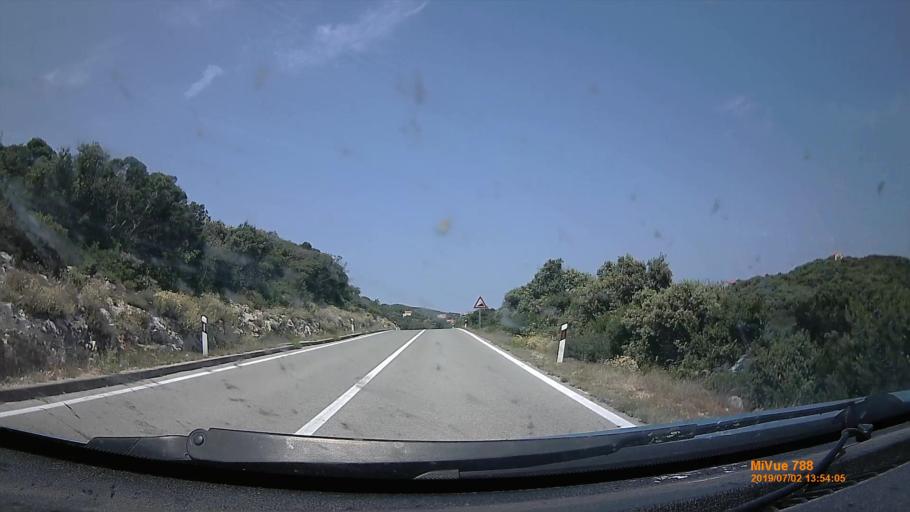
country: HR
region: Primorsko-Goranska
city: Mali Losinj
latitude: 44.6349
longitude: 14.3921
